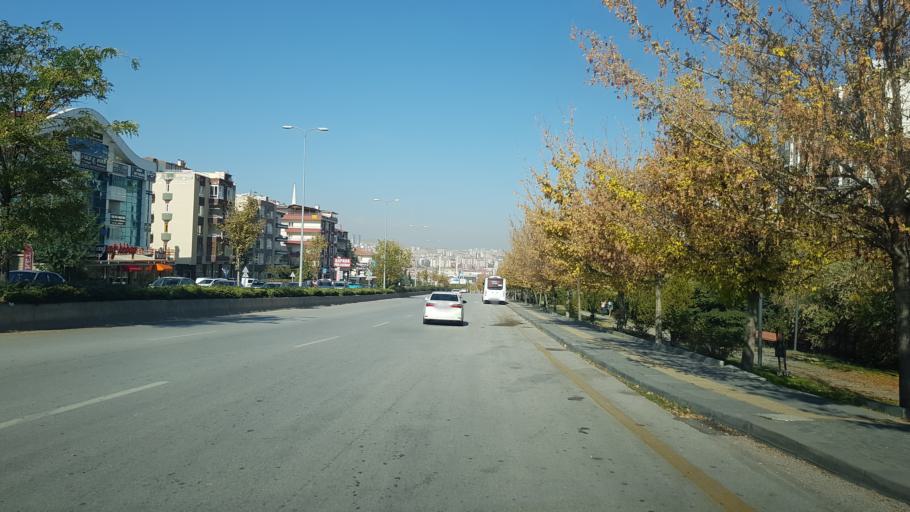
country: TR
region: Ankara
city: Etimesgut
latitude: 39.9528
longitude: 32.6047
